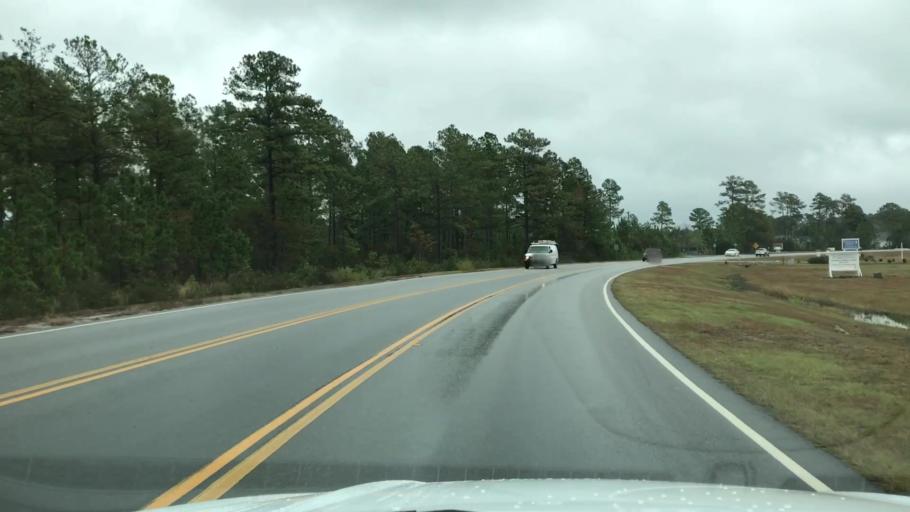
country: US
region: South Carolina
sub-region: Horry County
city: Myrtle Beach
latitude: 33.7615
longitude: -78.8886
